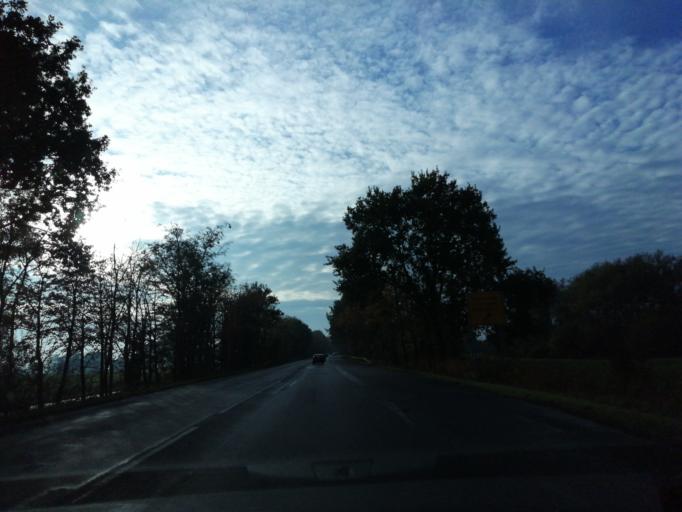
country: DE
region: Lower Saxony
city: Fedderwarden
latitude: 53.5984
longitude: 8.0509
